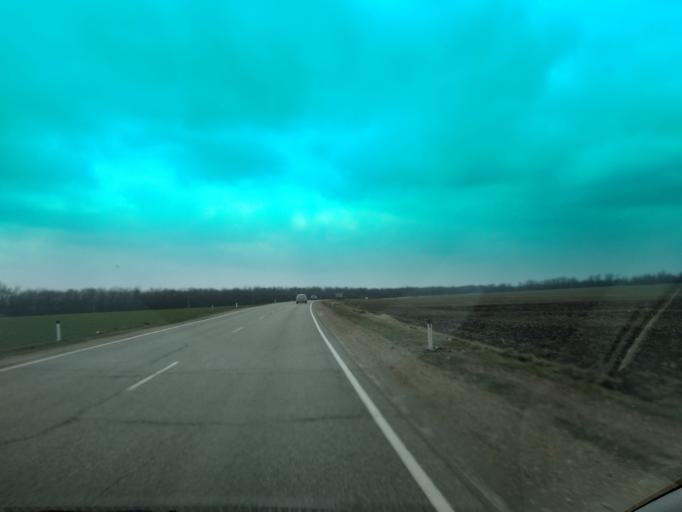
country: RU
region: Krasnodarskiy
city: Novomalorossiyskaya
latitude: 45.7316
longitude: 39.9073
